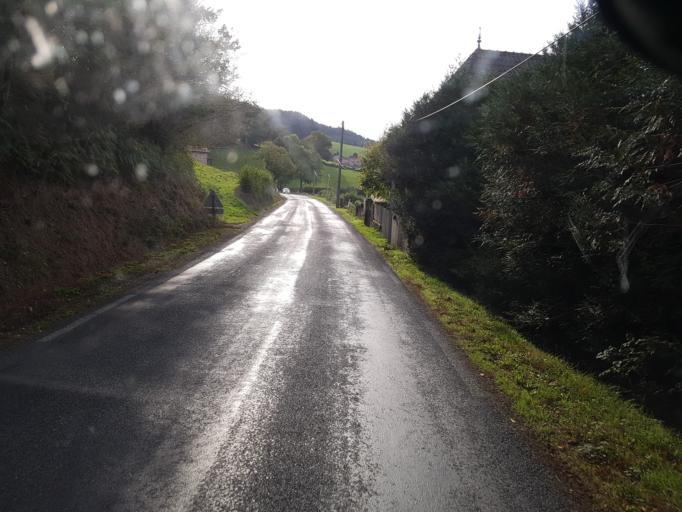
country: FR
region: Bourgogne
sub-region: Departement de Saone-et-Loire
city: Chauffailles
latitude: 46.2486
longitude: 4.4040
